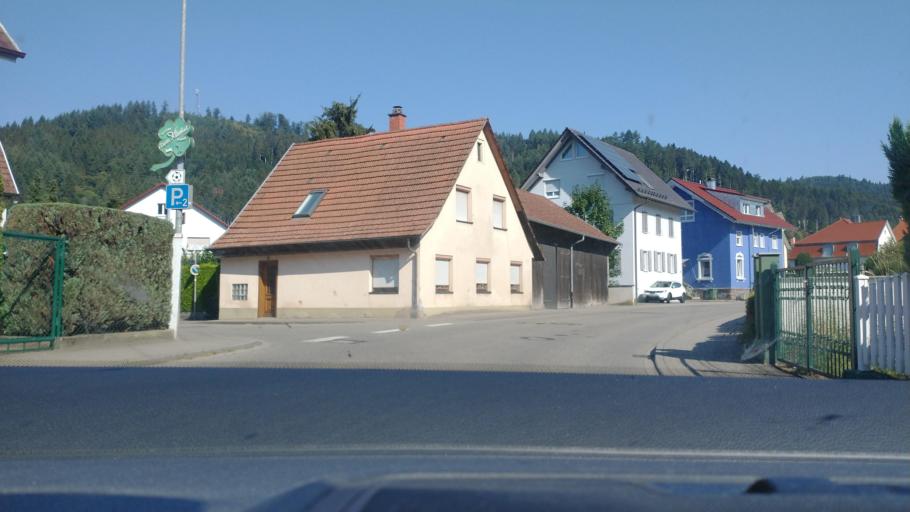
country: DE
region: Baden-Wuerttemberg
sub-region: Freiburg Region
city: Biberach
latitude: 48.3467
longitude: 8.0610
